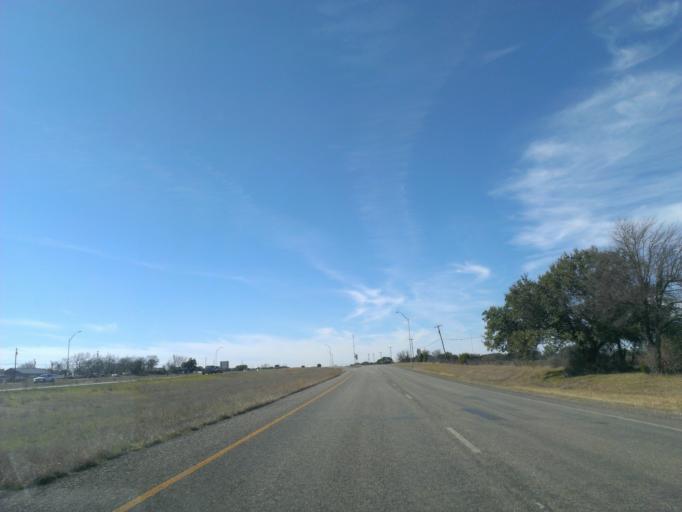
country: US
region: Texas
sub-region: Bell County
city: Belton
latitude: 31.0559
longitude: -97.5098
